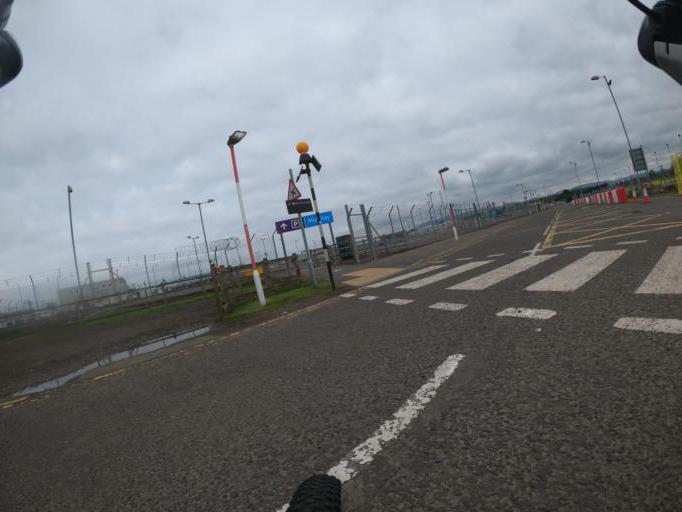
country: GB
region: Scotland
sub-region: Edinburgh
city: Ratho
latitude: 55.9467
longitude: -3.3585
